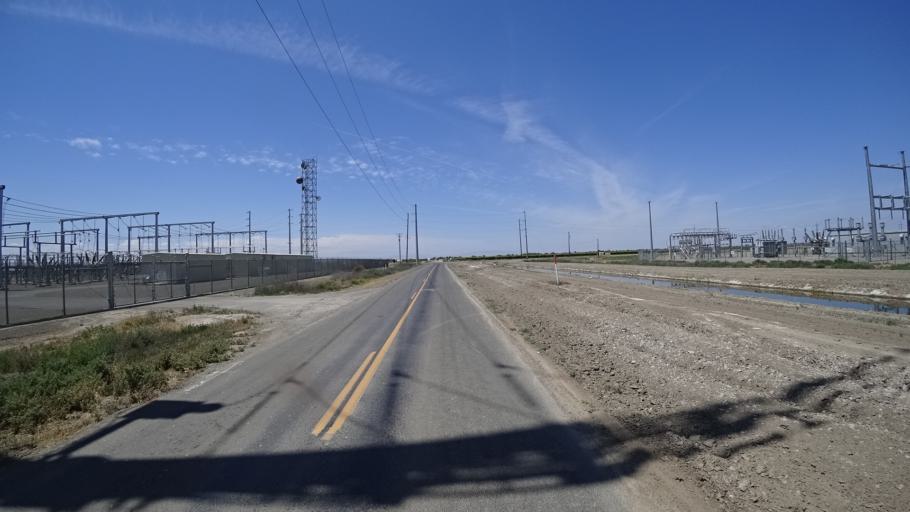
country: US
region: California
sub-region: Kings County
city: Stratford
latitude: 36.2407
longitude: -119.8326
